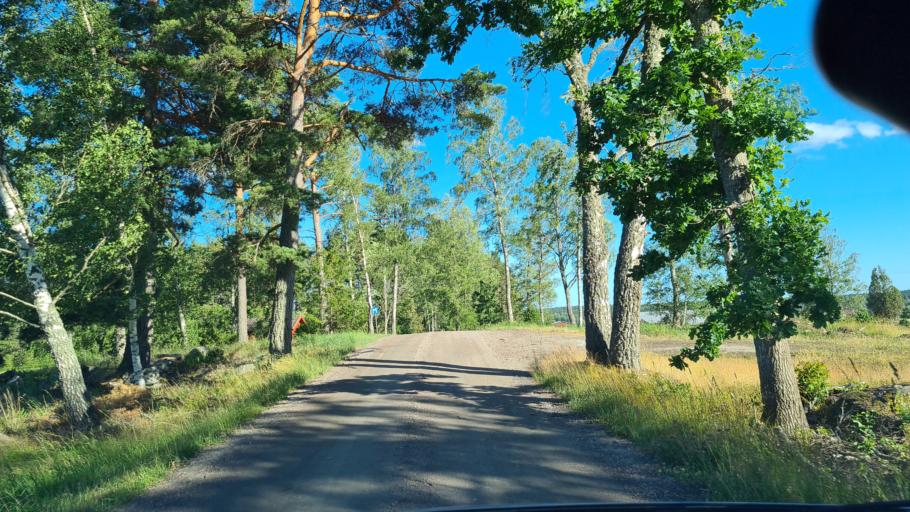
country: SE
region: Soedermanland
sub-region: Nykopings Kommun
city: Nykoping
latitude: 58.9080
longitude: 16.9561
